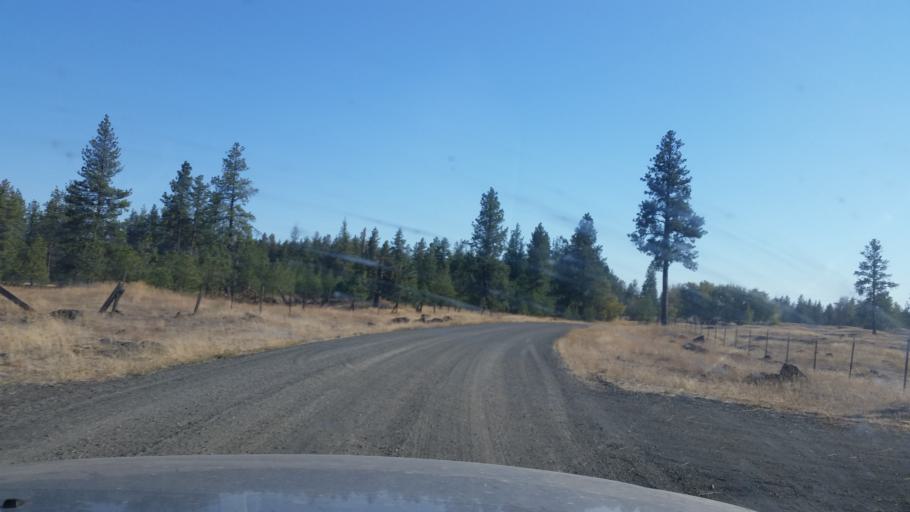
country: US
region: Washington
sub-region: Spokane County
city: Cheney
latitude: 47.4270
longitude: -117.6512
